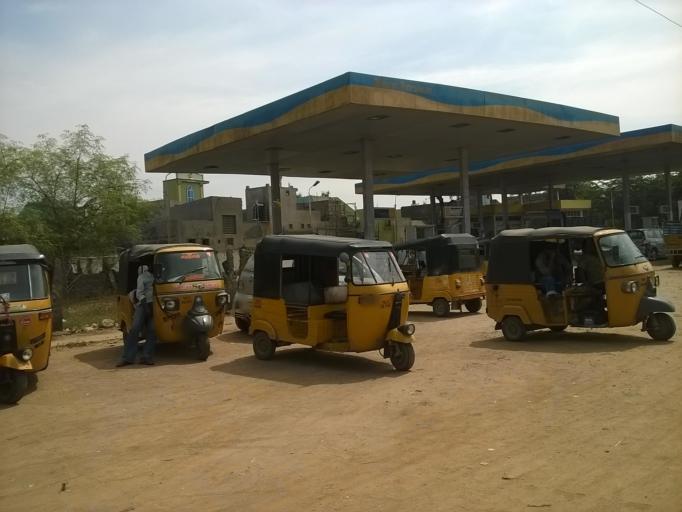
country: IN
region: Tamil Nadu
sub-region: Cuddalore
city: Panruti
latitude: 11.7678
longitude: 79.5499
